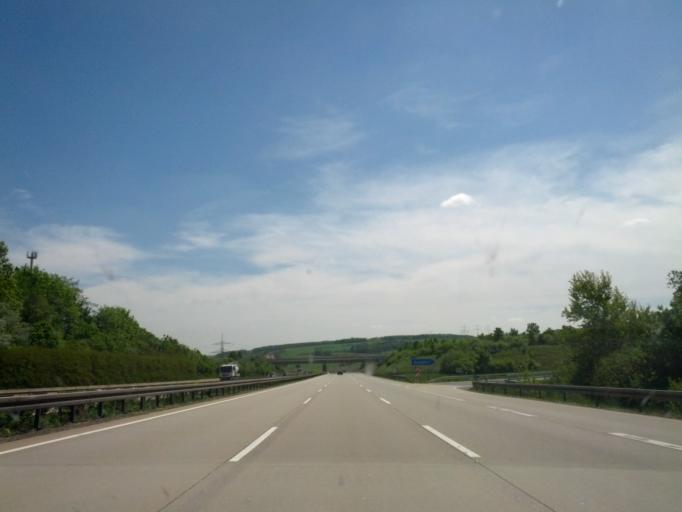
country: DE
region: Thuringia
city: Magdala
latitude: 50.8990
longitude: 11.4365
